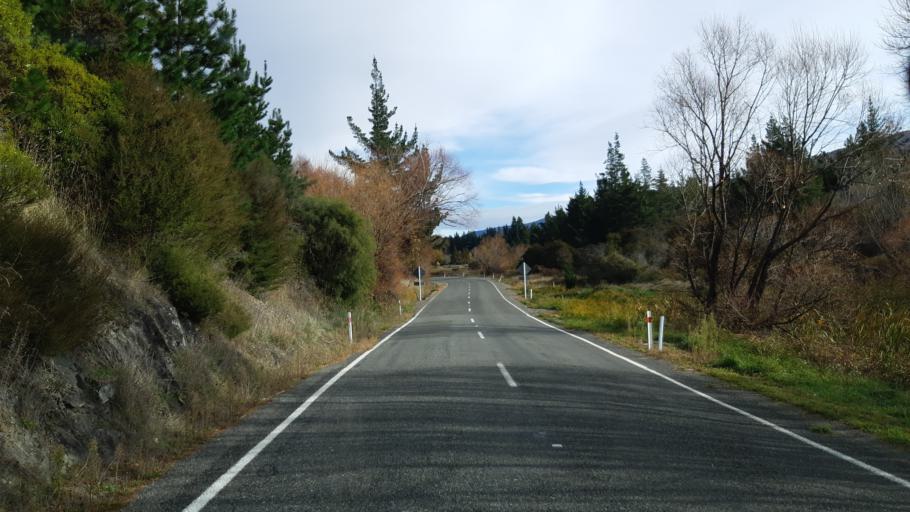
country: NZ
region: Tasman
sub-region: Tasman District
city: Wakefield
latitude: -41.7178
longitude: 173.1055
